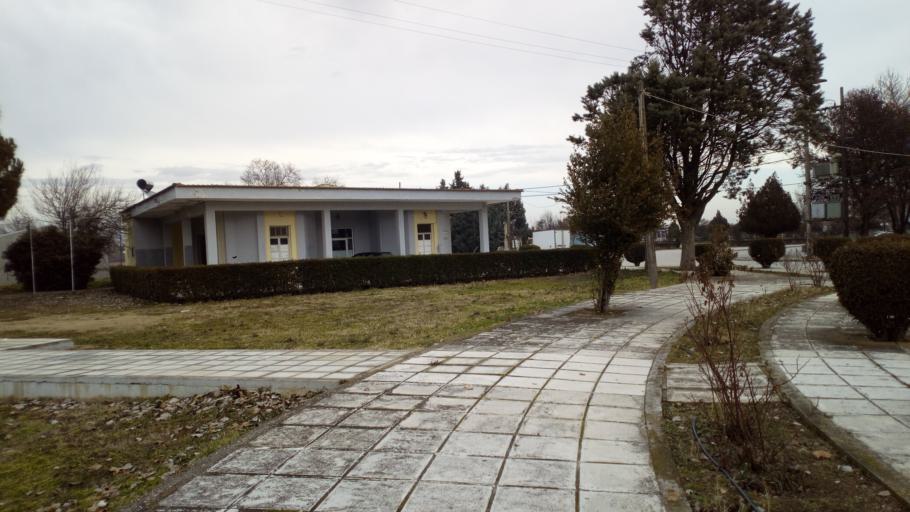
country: GR
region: Central Macedonia
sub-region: Nomos Thessalonikis
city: Lagkadas
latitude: 40.7340
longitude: 23.0851
